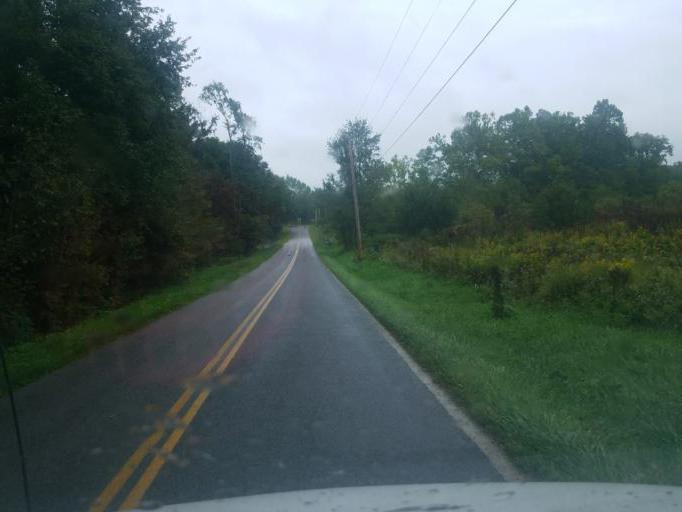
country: US
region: Ohio
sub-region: Medina County
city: Seville
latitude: 41.0452
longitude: -81.8490
